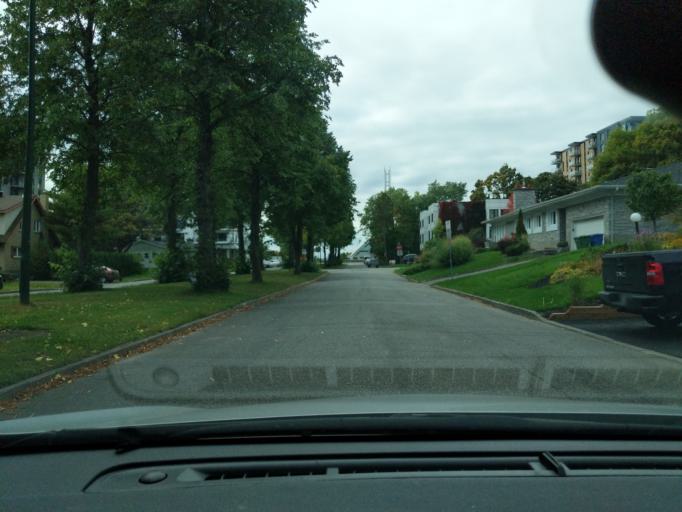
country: CA
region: Quebec
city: L'Ancienne-Lorette
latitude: 46.7716
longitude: -71.2917
